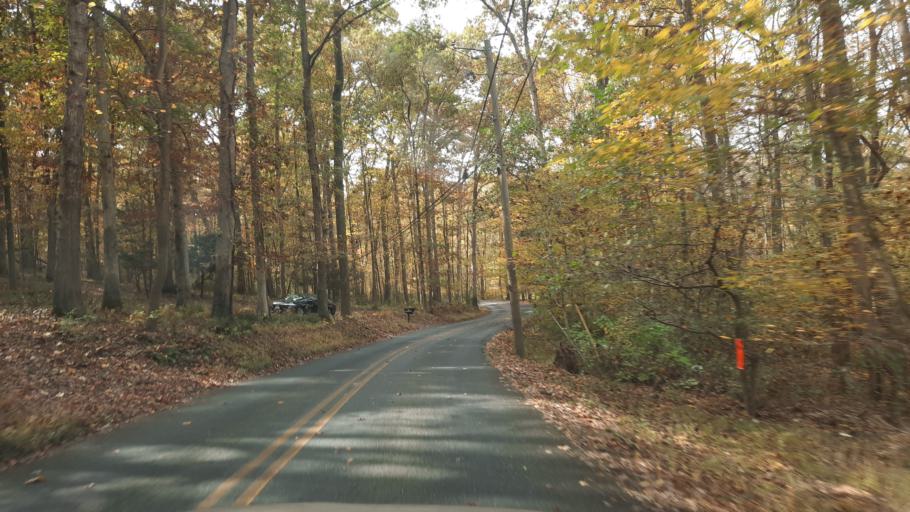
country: US
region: Maryland
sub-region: Montgomery County
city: Germantown
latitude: 39.1594
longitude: -77.2371
